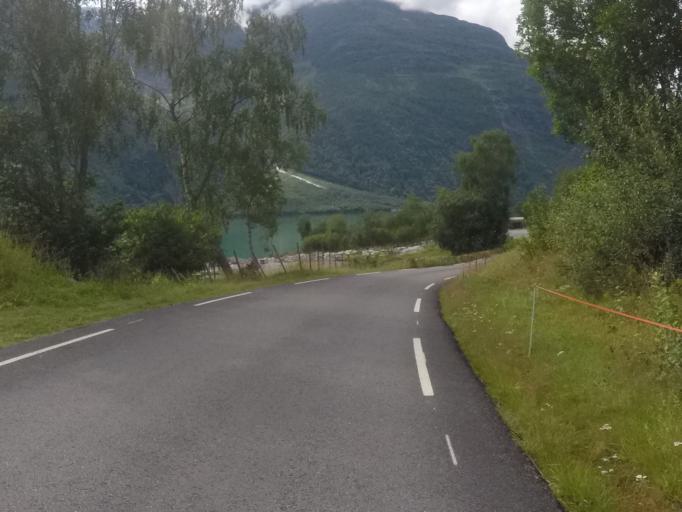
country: NO
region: Sogn og Fjordane
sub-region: Stryn
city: Stryn
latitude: 61.8252
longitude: 6.9733
